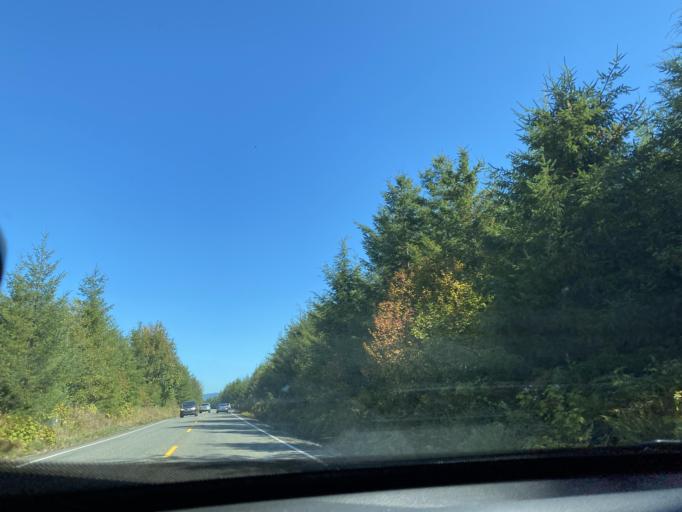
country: US
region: Washington
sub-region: Clallam County
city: Forks
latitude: 47.9289
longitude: -124.4857
